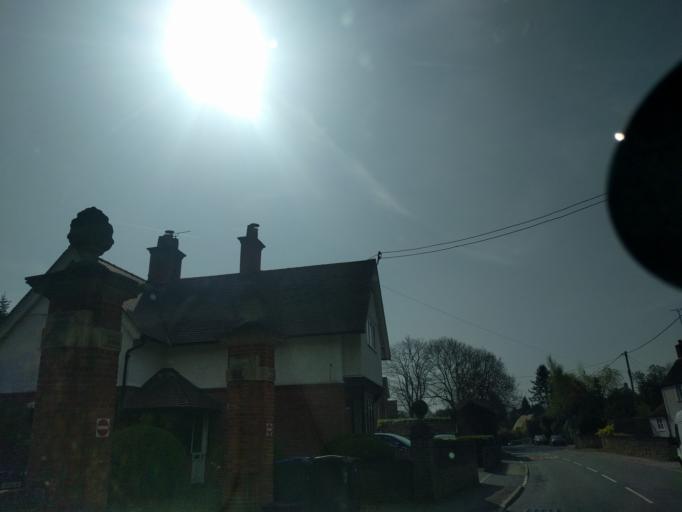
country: GB
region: England
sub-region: Wiltshire
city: Market Lavington
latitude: 51.2882
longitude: -2.0051
